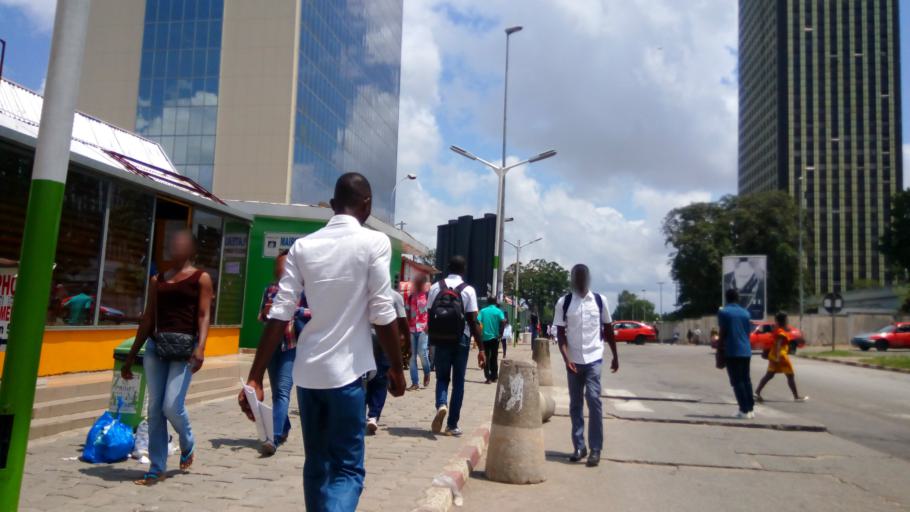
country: CI
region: Lagunes
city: Abidjan
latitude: 5.3317
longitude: -4.0211
